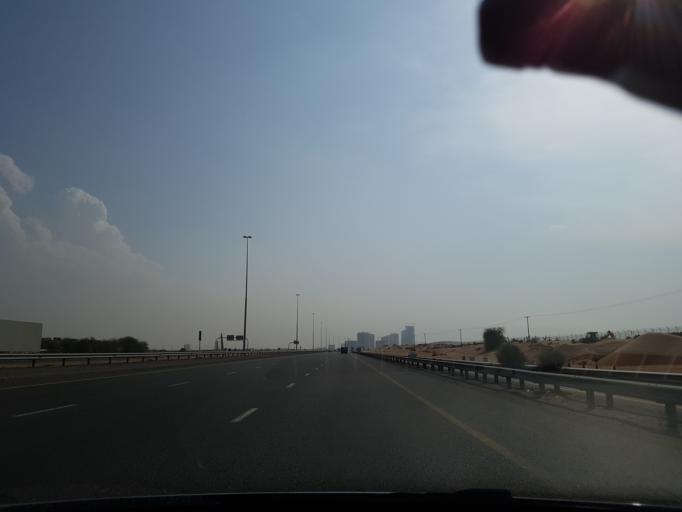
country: AE
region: Umm al Qaywayn
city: Umm al Qaywayn
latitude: 25.4207
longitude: 55.5902
